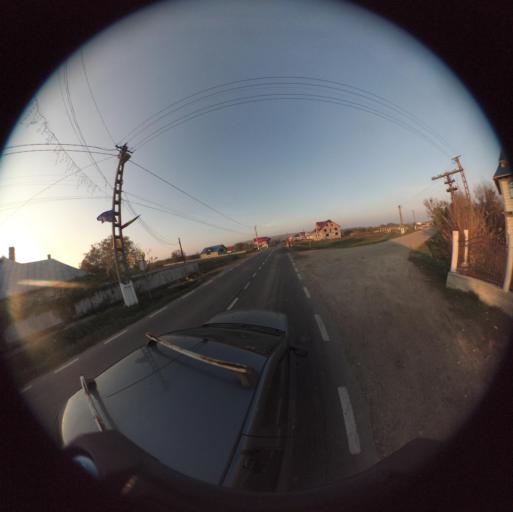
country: RO
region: Vaslui
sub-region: Comuna Bacesti
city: Bacesti
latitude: 46.8268
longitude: 27.2506
